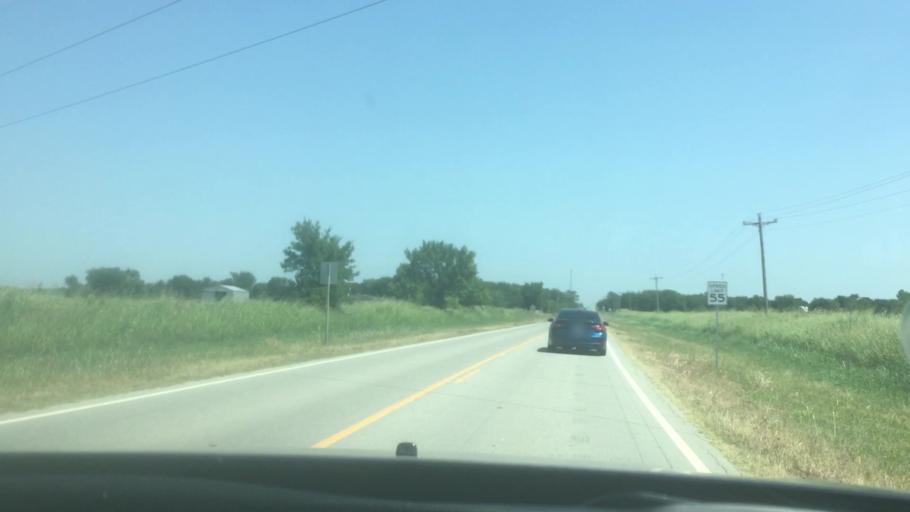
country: US
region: Oklahoma
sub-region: Coal County
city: Coalgate
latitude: 34.5951
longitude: -96.4244
